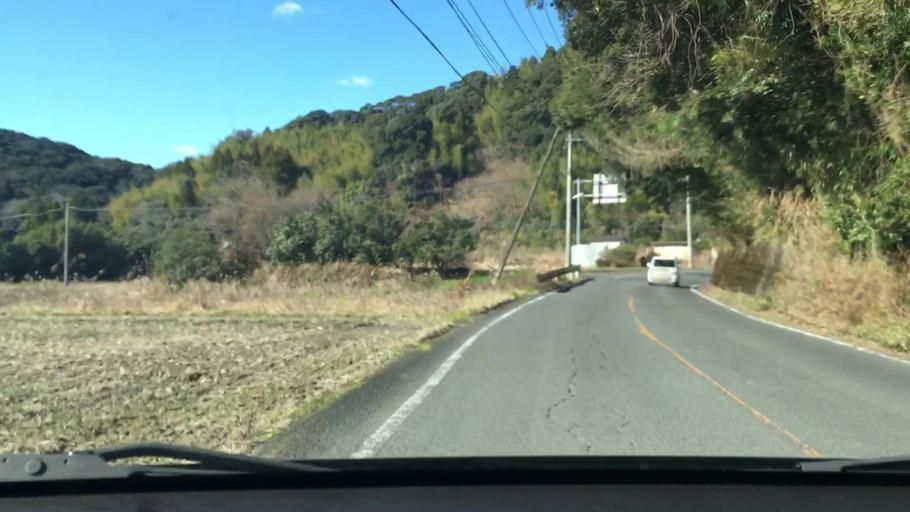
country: JP
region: Kagoshima
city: Satsumasendai
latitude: 31.7799
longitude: 130.3993
